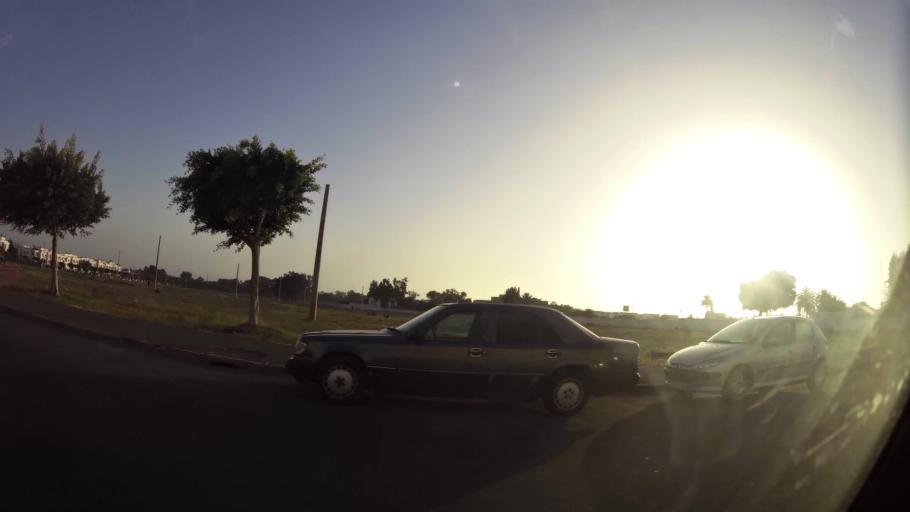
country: MA
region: Oued ed Dahab-Lagouira
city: Dakhla
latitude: 30.3942
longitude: -9.5733
